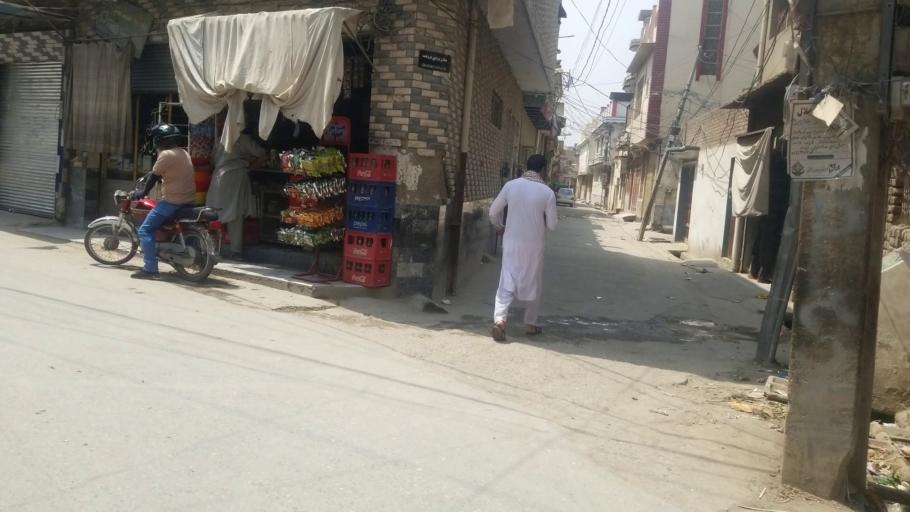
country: PK
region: Khyber Pakhtunkhwa
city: Peshawar
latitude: 34.0288
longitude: 71.5886
